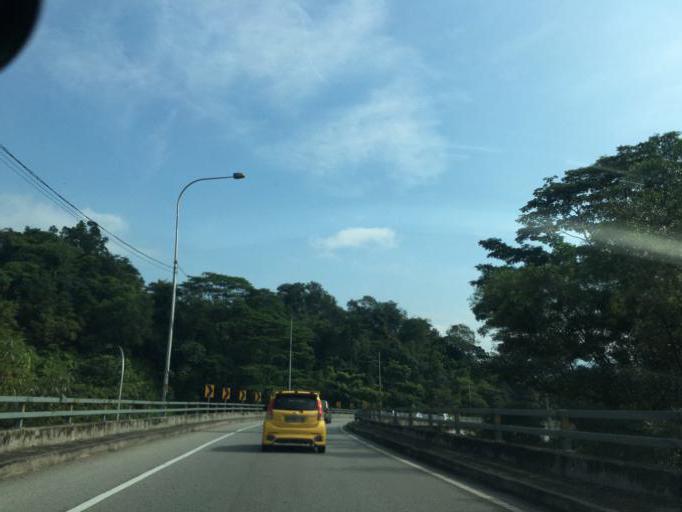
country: MY
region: Kuala Lumpur
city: Kuala Lumpur
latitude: 3.2403
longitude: 101.7212
